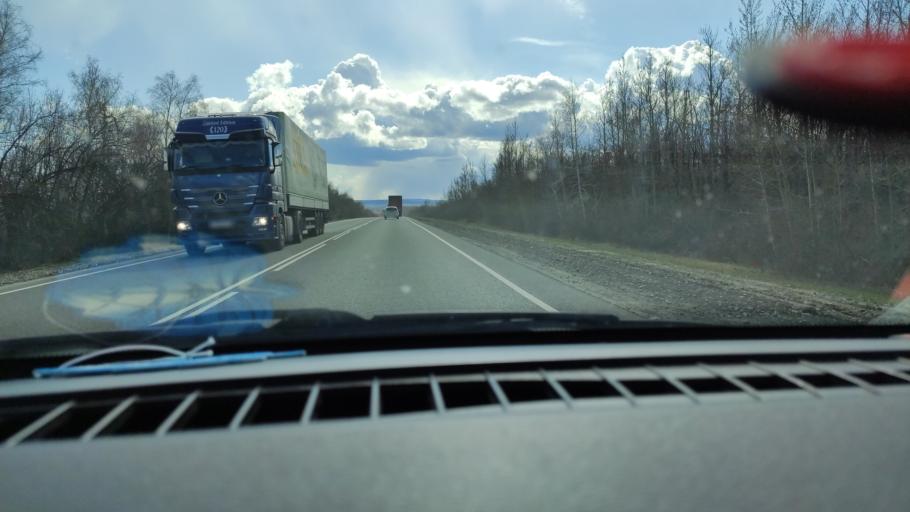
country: RU
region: Saratov
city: Dukhovnitskoye
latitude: 52.6194
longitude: 48.1711
